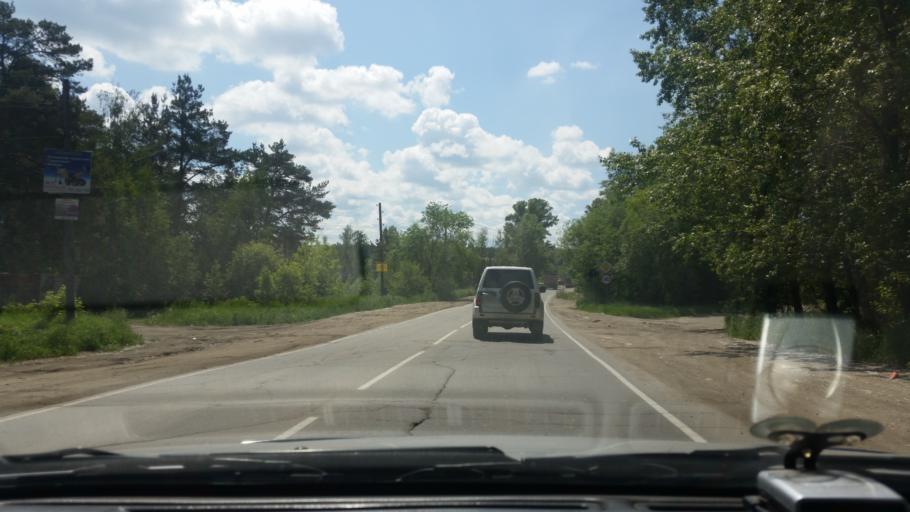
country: RU
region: Irkutsk
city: Shelekhov
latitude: 52.2106
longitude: 104.1108
